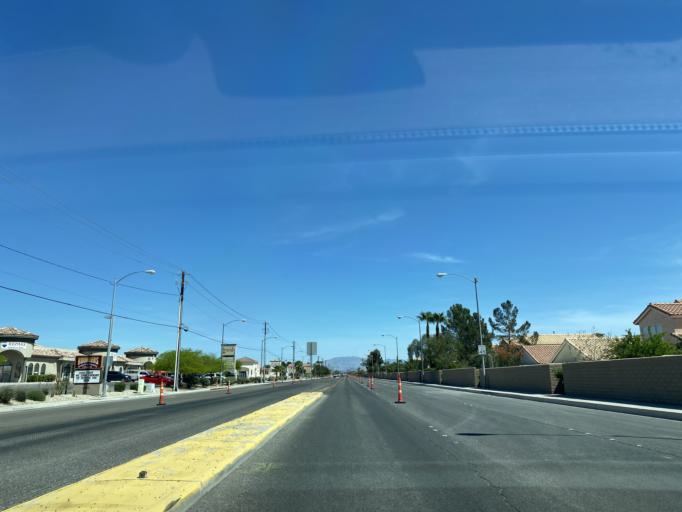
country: US
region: Nevada
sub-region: Clark County
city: Spring Valley
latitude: 36.1074
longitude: -115.2610
